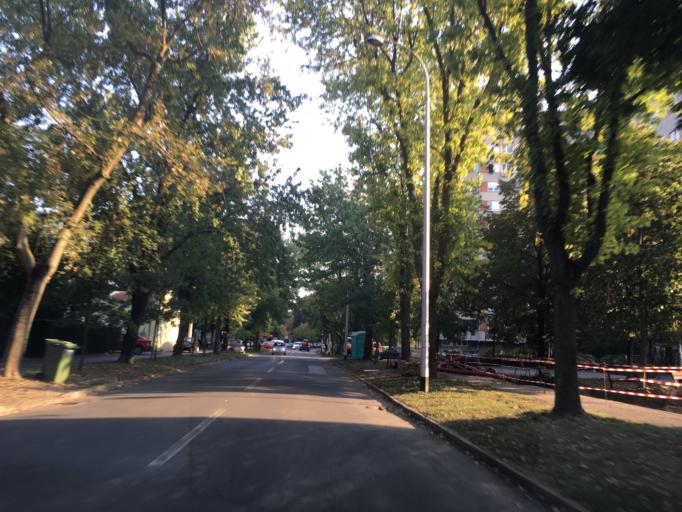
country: HR
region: Grad Zagreb
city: Jankomir
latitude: 45.7922
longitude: 15.9411
